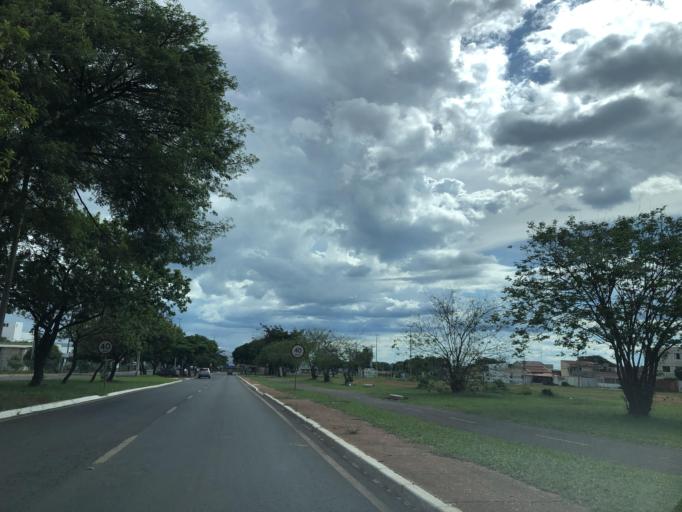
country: BR
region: Goias
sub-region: Luziania
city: Luziania
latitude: -16.0215
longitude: -48.0692
